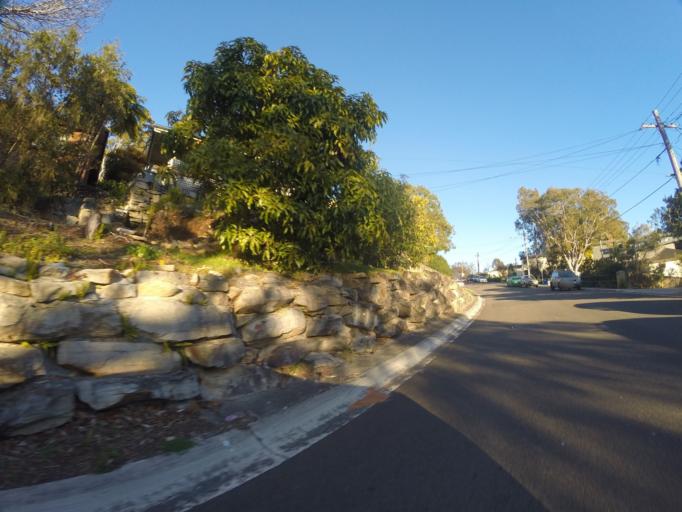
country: AU
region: New South Wales
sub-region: Sutherland Shire
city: Grays Point
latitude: -34.0583
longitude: 151.0747
